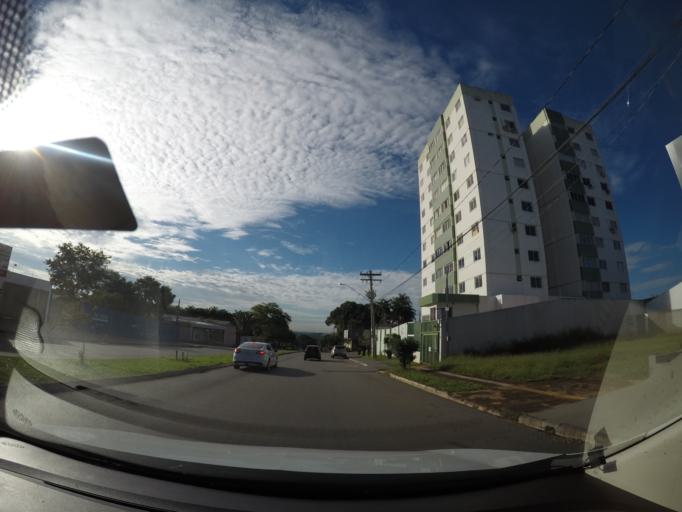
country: BR
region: Goias
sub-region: Goiania
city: Goiania
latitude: -16.7417
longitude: -49.2714
